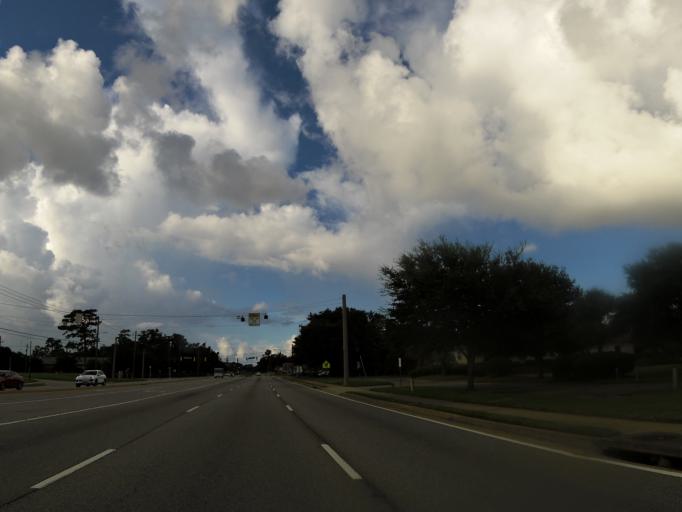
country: US
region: Georgia
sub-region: Glynn County
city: Brunswick
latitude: 31.1709
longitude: -81.4744
